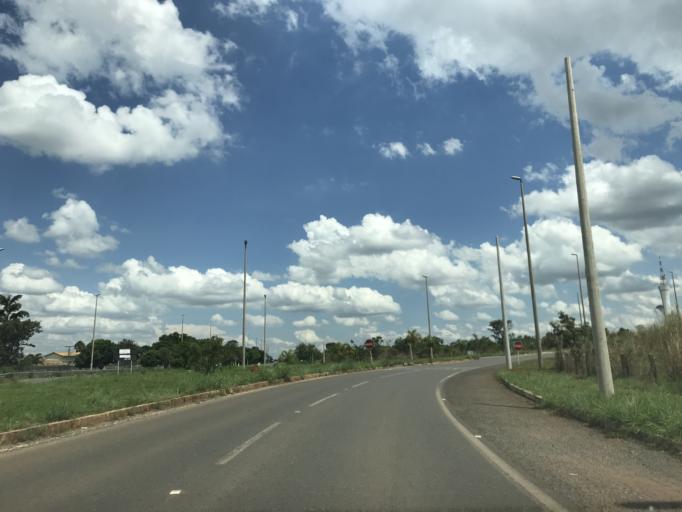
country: BR
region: Federal District
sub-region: Brasilia
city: Brasilia
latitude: -15.6890
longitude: -47.8350
